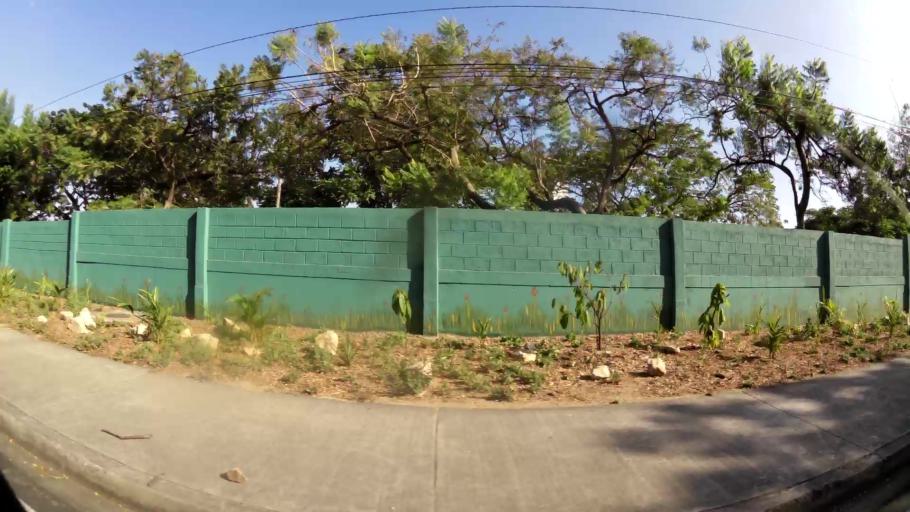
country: EC
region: Guayas
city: Santa Lucia
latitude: -2.1865
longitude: -79.9661
